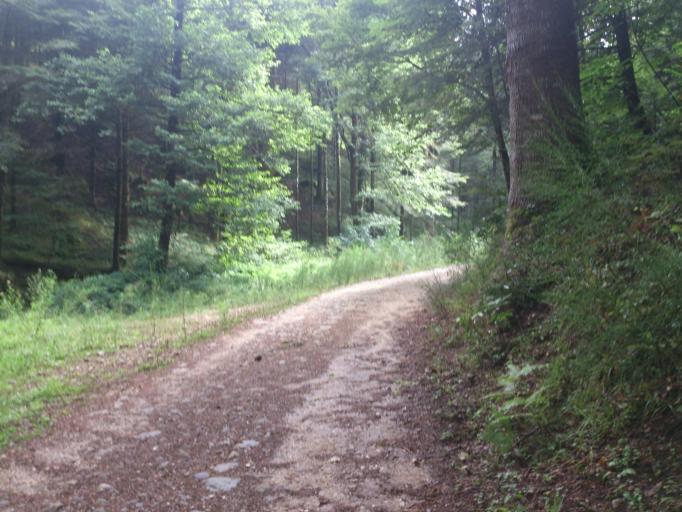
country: IT
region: Calabria
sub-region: Provincia di Vibo-Valentia
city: Serra San Bruno
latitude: 38.5488
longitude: 16.3099
